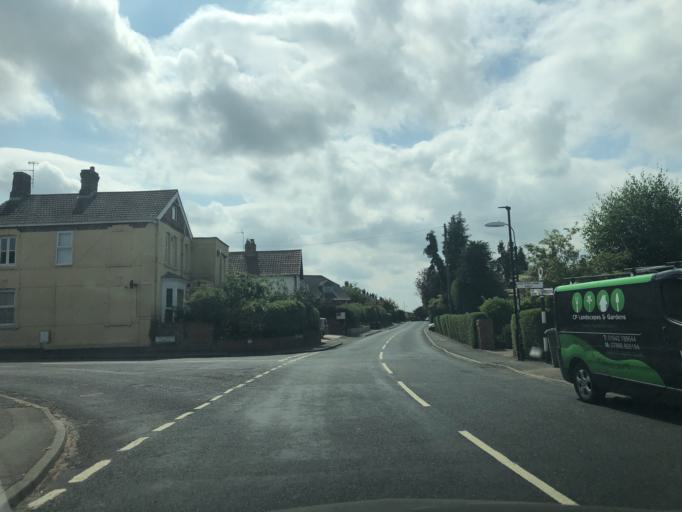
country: GB
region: England
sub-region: Redcar and Cleveland
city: Thornaby-on-Tees
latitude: 54.4499
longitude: -1.2825
